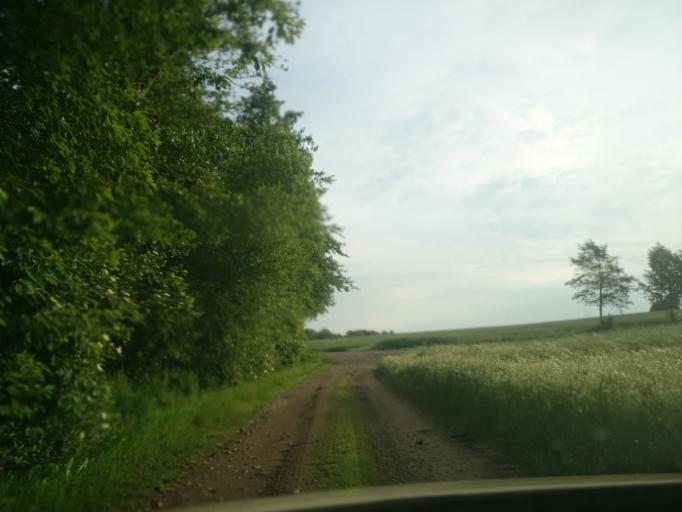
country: DE
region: Saxony
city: Eppendorf
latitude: 50.8360
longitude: 13.2387
